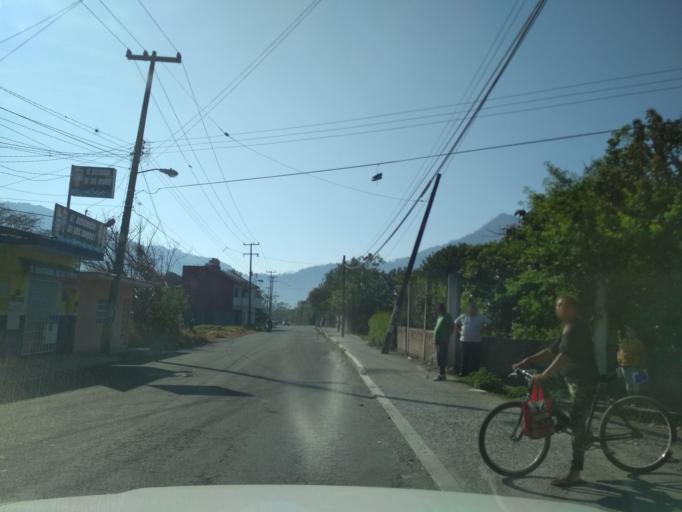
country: MX
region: Veracruz
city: Jalapilla
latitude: 18.8217
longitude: -97.0829
